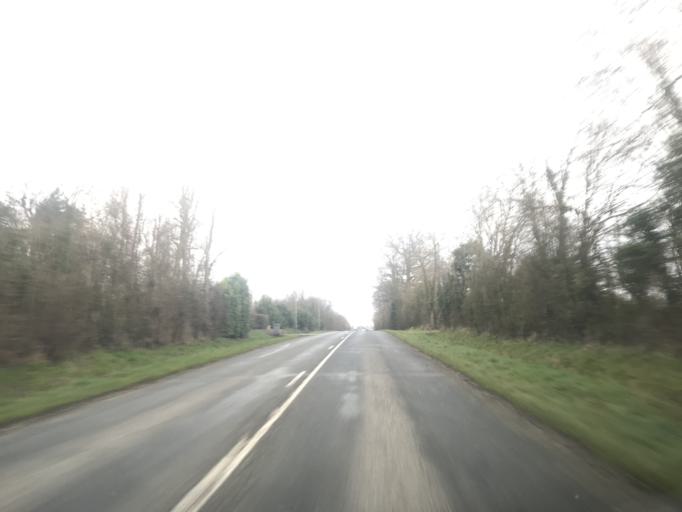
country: FR
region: Lower Normandy
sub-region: Departement du Calvados
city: Troarn
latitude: 49.2084
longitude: -0.1181
